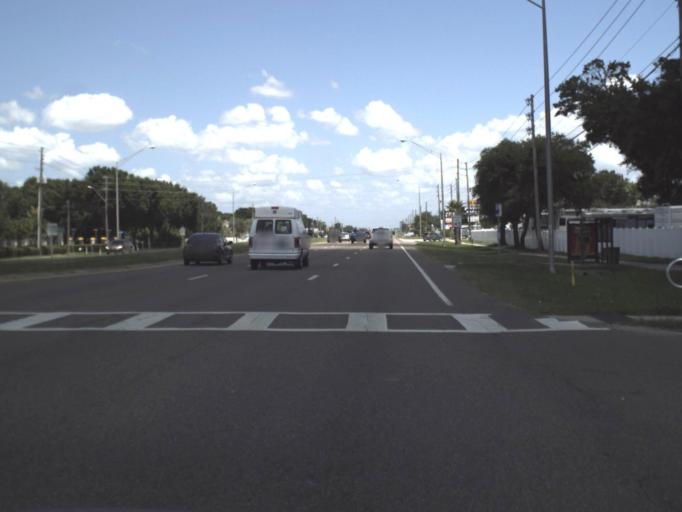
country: US
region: Florida
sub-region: Pinellas County
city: South Highpoint
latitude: 27.8791
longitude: -82.7290
